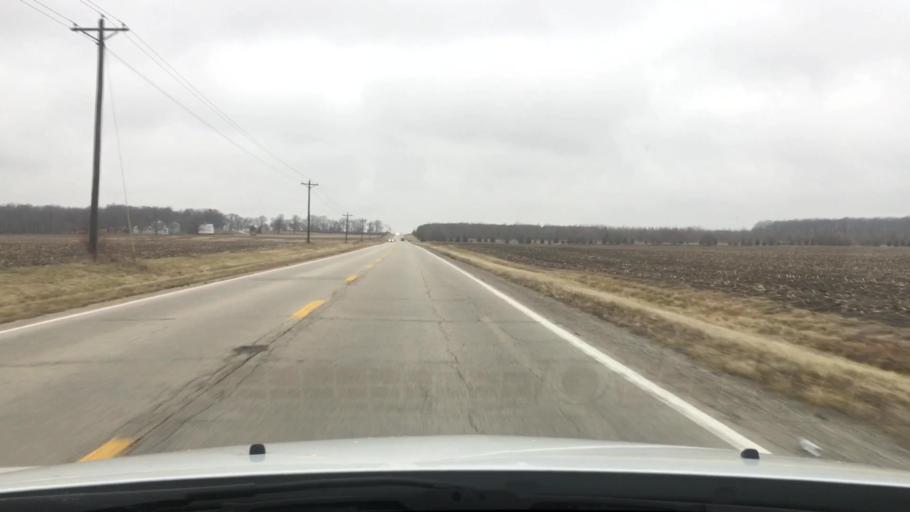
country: US
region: Illinois
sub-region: Iroquois County
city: Watseka
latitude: 40.8916
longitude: -87.6774
